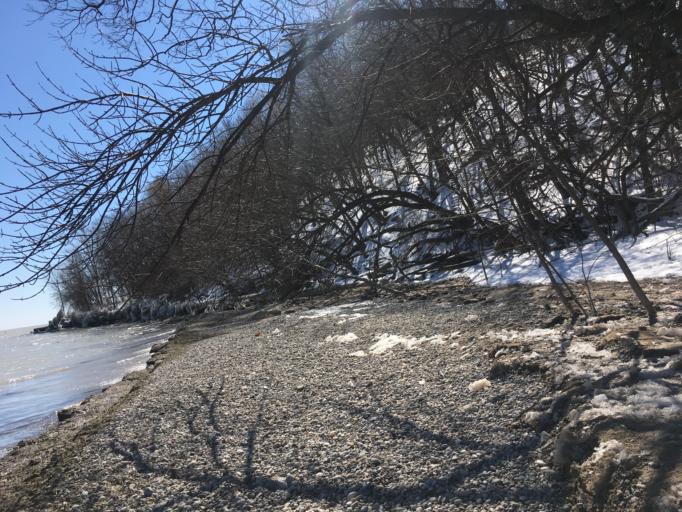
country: US
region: Wisconsin
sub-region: Milwaukee County
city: Shorewood
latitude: 43.0890
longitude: -87.8723
